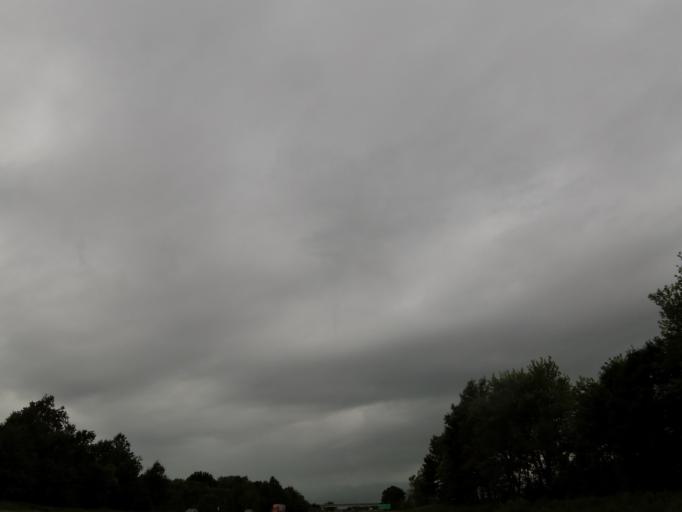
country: US
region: Illinois
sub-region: Clinton County
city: Wamac
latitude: 38.3896
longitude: -89.1857
